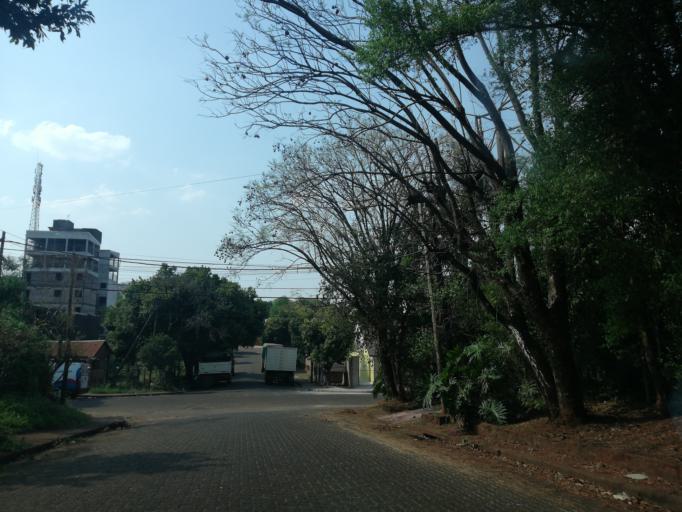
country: AR
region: Misiones
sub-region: Departamento de Capital
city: Posadas
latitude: -27.4026
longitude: -55.9073
